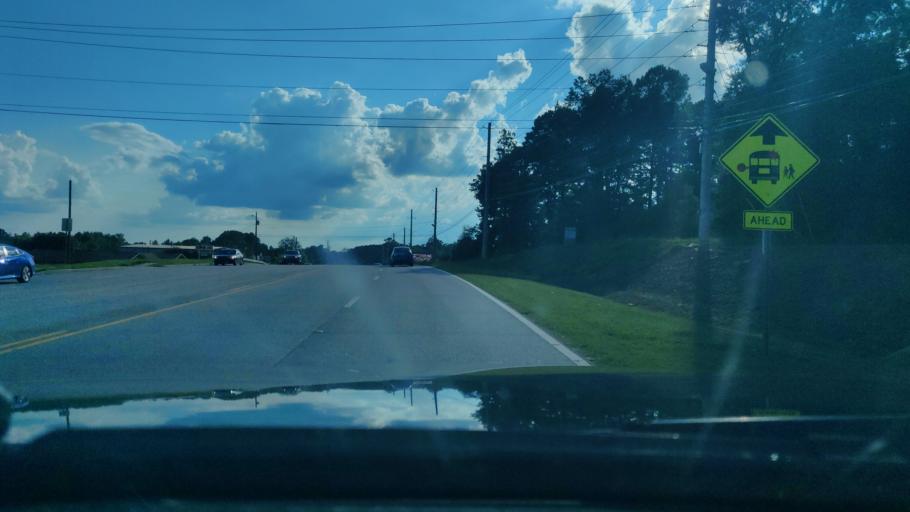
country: US
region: Alabama
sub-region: Lee County
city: Opelika
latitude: 32.6219
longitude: -85.4123
